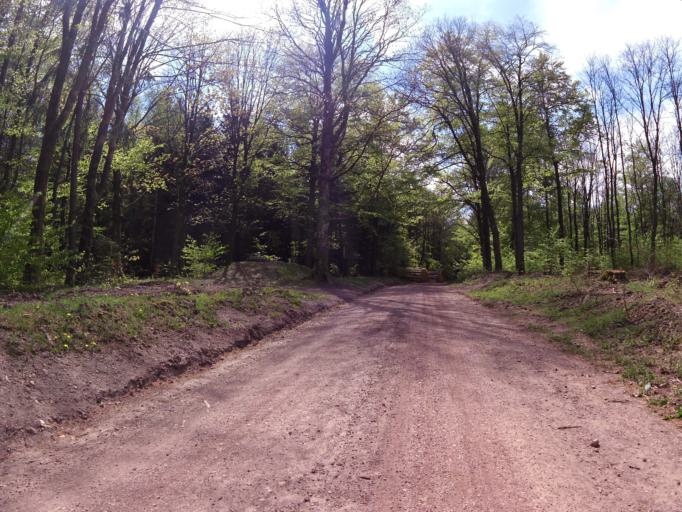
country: DE
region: Thuringia
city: Ruhla
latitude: 50.9000
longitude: 10.3374
